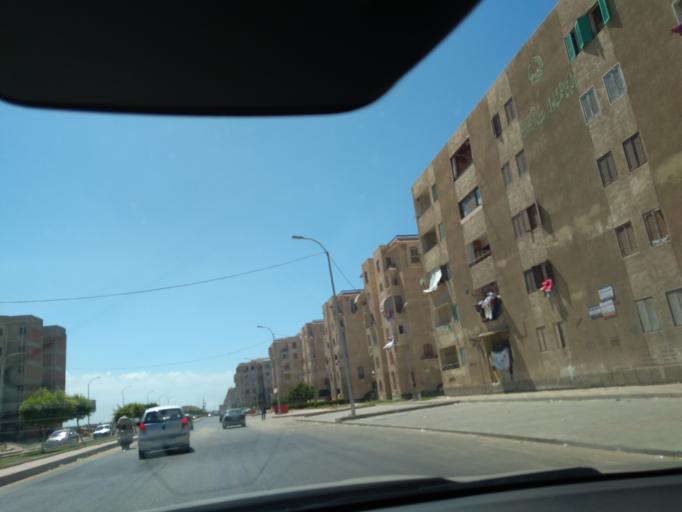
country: EG
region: Dumyat
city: Faraskur
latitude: 31.4244
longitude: 31.6727
